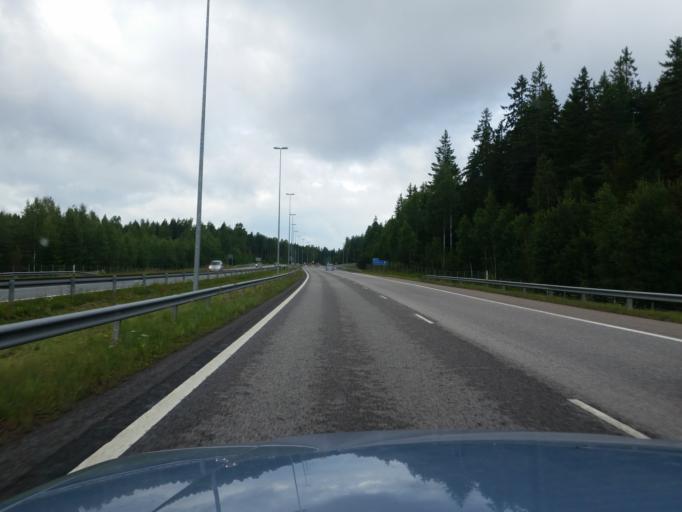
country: FI
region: Uusimaa
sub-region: Helsinki
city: Kirkkonummi
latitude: 60.2701
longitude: 24.4658
